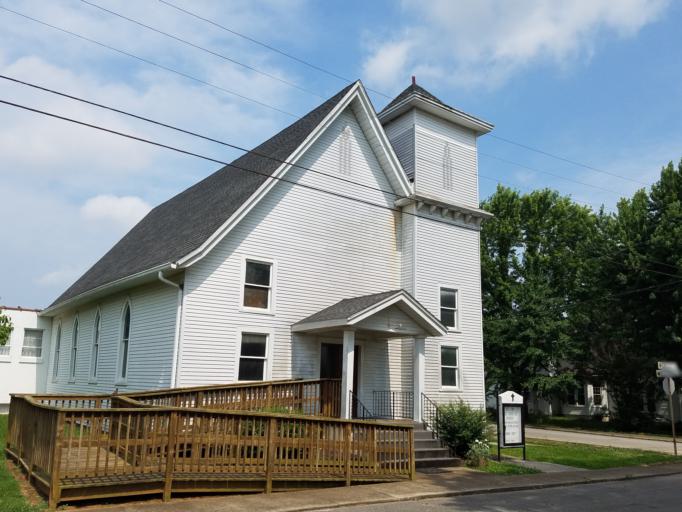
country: US
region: Kentucky
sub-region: Edmonson County
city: Brownsville
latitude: 37.0567
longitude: -86.2062
